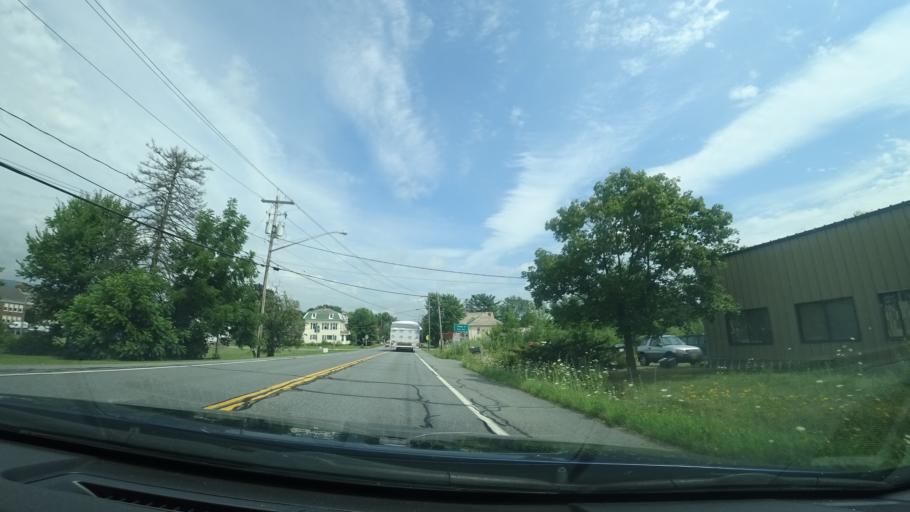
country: US
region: New York
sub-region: Warren County
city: Queensbury
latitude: 43.4094
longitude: -73.4894
